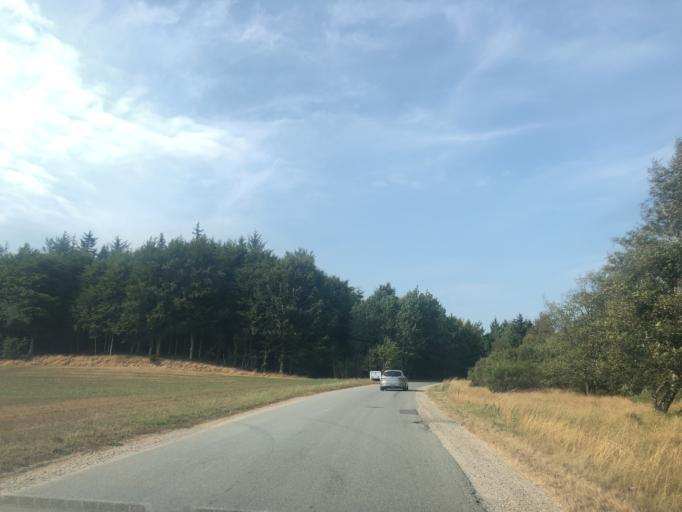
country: DK
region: North Denmark
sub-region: Morso Kommune
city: Nykobing Mors
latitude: 56.8381
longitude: 9.0454
